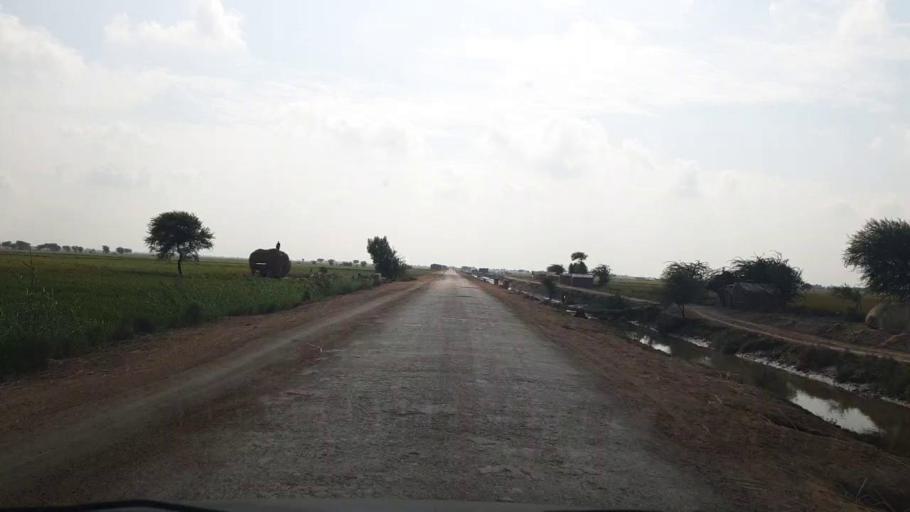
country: PK
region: Sindh
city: Kario
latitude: 24.5854
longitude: 68.5759
